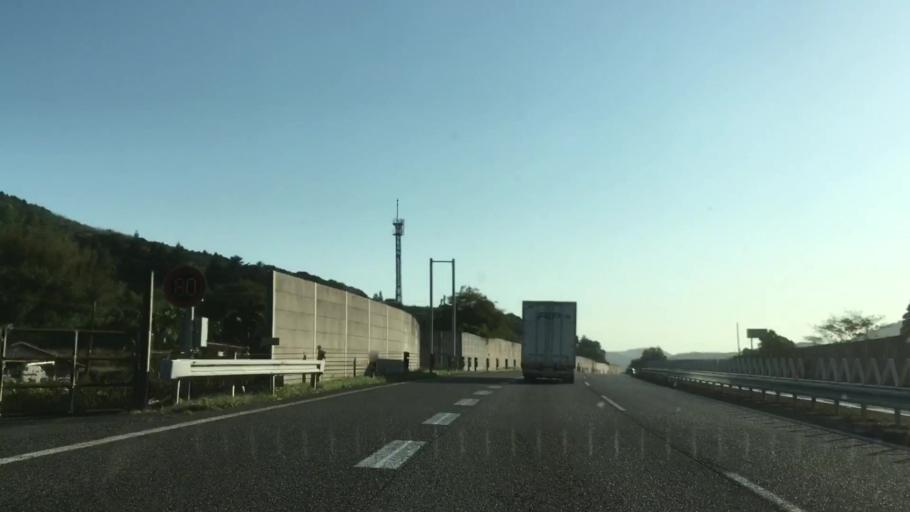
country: JP
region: Yamaguchi
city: Onoda
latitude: 34.1467
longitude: 131.2332
